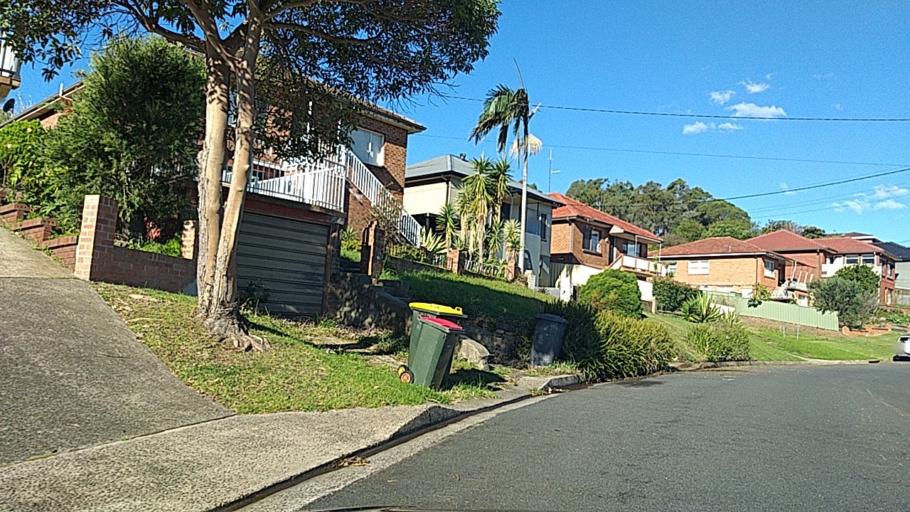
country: AU
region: New South Wales
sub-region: Wollongong
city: Port Kembla
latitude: -34.4826
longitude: 150.8917
